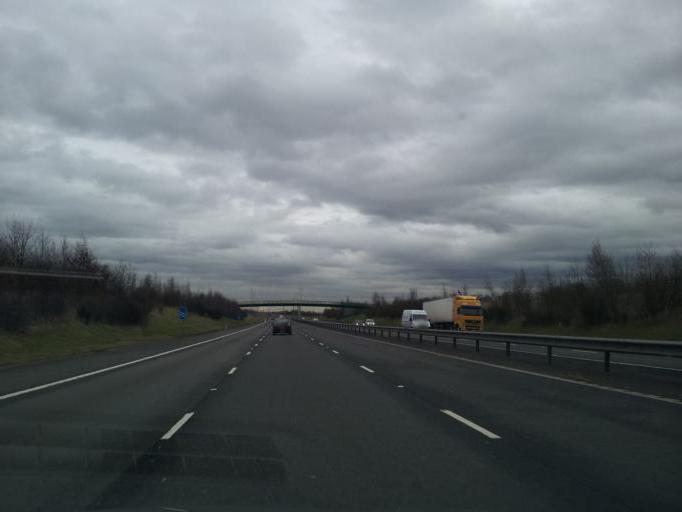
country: GB
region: England
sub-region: Warwickshire
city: Curdworth
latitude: 52.5536
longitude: -1.7411
